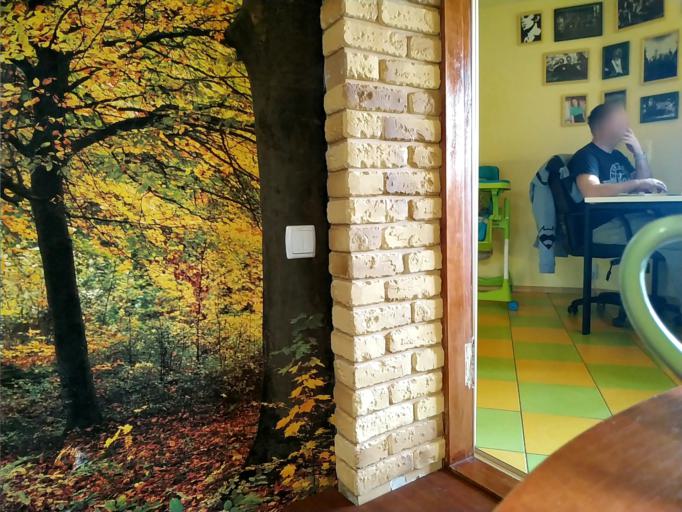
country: RU
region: Jaroslavl
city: Krasnyy Profintern
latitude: 57.9002
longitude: 40.5773
